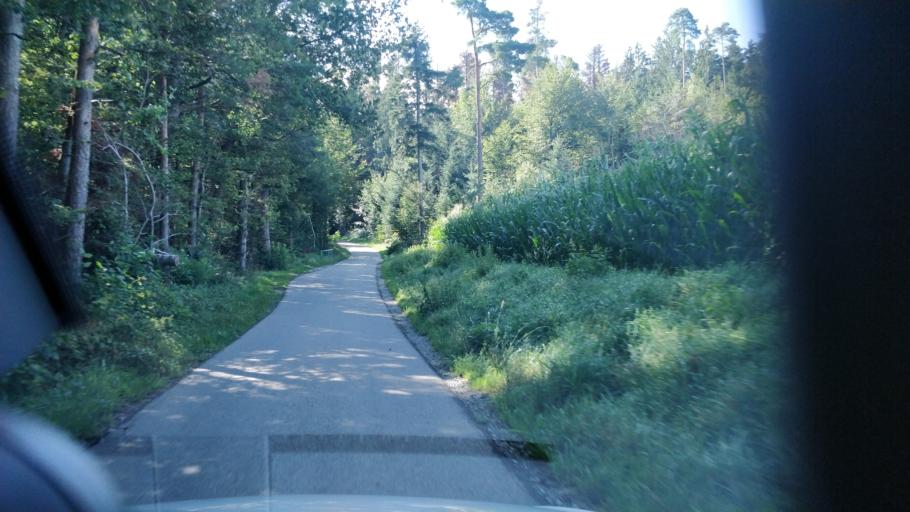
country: DE
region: Baden-Wuerttemberg
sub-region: Regierungsbezirk Stuttgart
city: Oberrot
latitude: 49.0034
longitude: 9.6508
